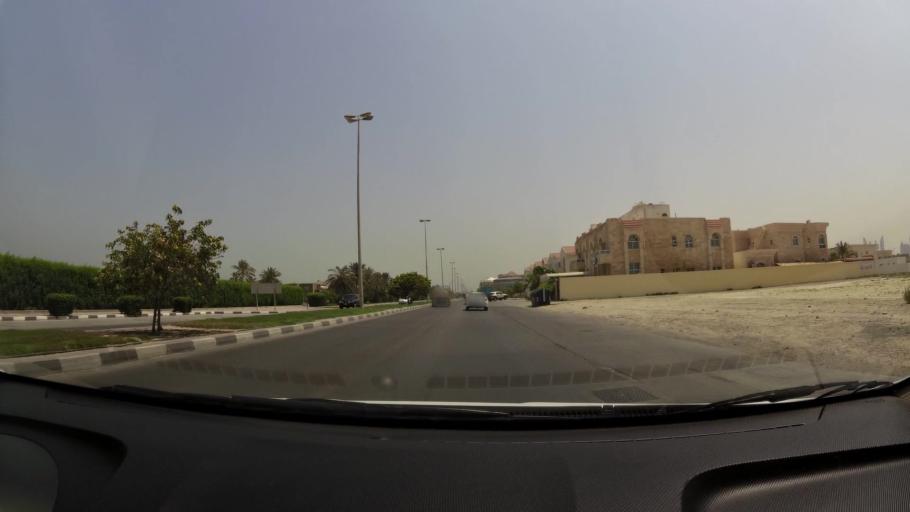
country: AE
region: Ash Shariqah
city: Sharjah
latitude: 25.3425
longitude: 55.3655
